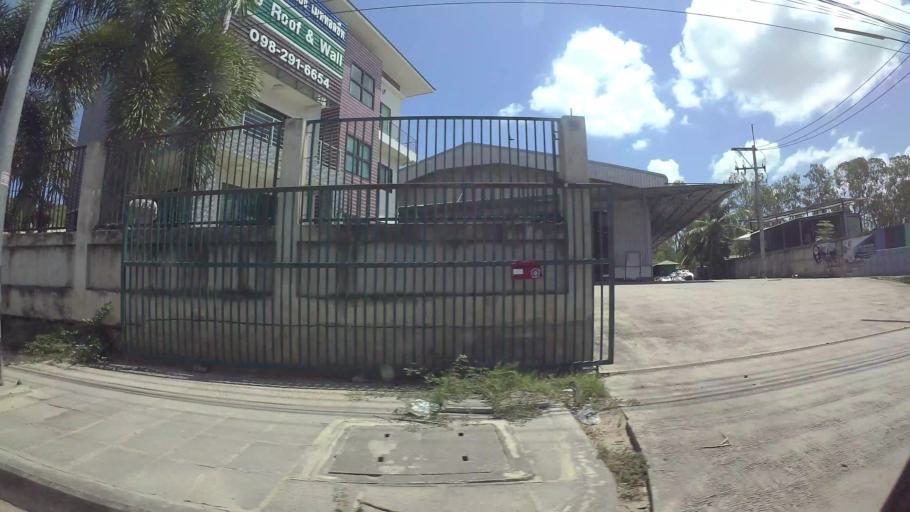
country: TH
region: Chon Buri
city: Ban Talat Bueng
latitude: 13.1125
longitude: 100.9550
